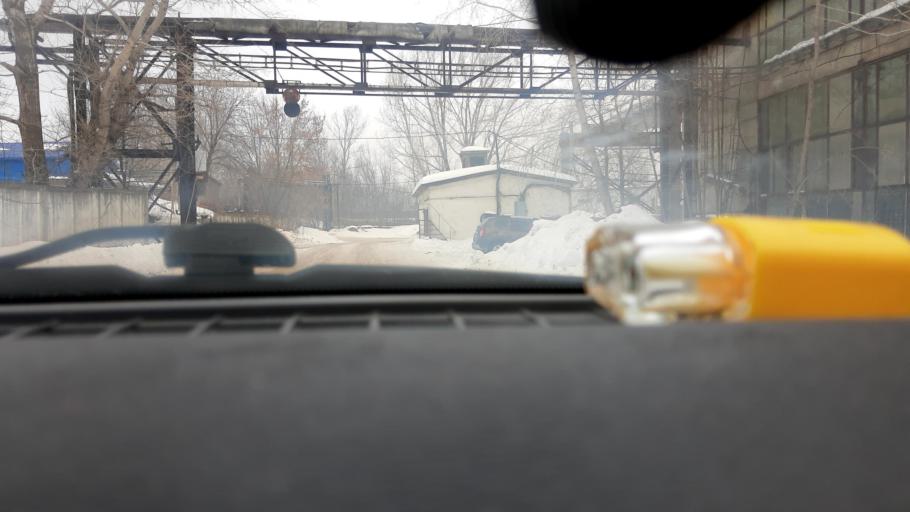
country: RU
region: Bashkortostan
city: Ufa
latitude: 54.8335
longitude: 56.1106
